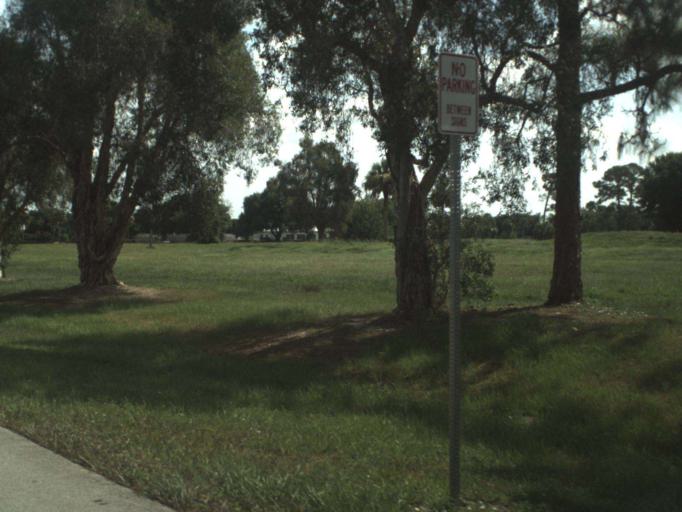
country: US
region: Florida
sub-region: Indian River County
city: Vero Beach South
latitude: 27.6434
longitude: -80.4302
